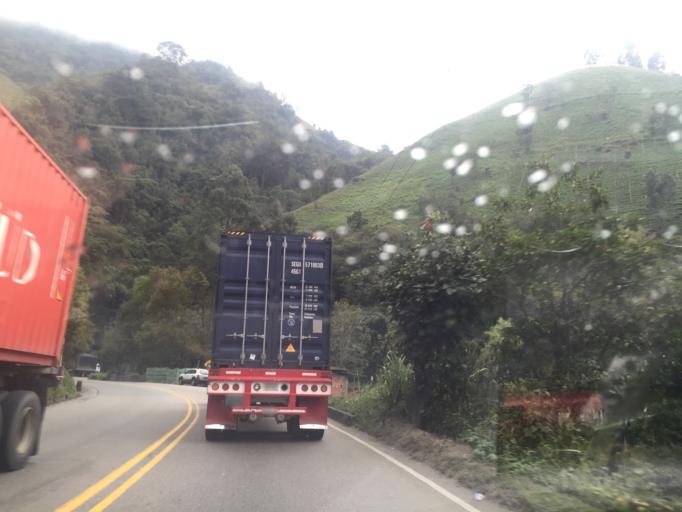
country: CO
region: Tolima
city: Cajamarca
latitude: 4.4339
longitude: -75.4647
